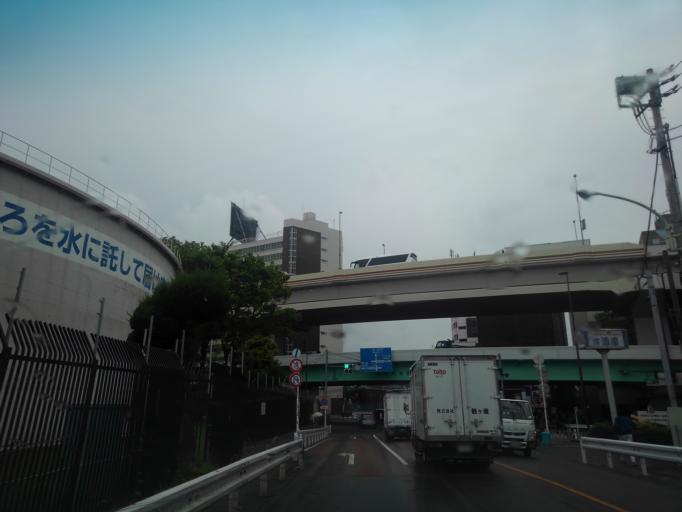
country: JP
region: Tokyo
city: Tokyo
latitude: 35.6712
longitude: 139.6525
